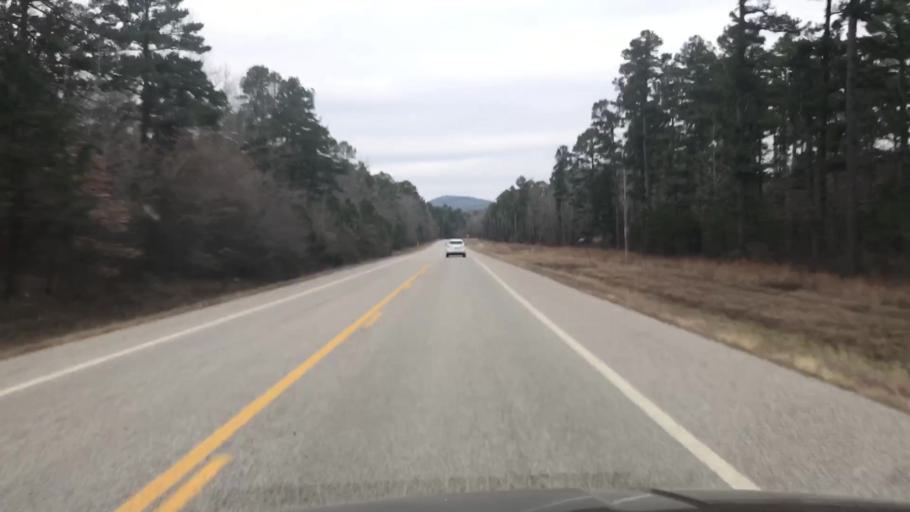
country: US
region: Arkansas
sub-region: Scott County
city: Waldron
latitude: 34.7124
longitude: -93.9419
